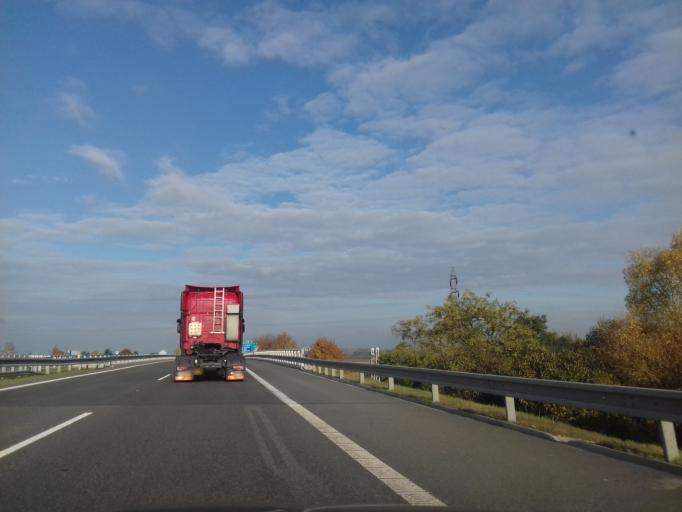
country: CZ
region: South Moravian
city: Hrusky
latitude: 48.7807
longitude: 16.9281
